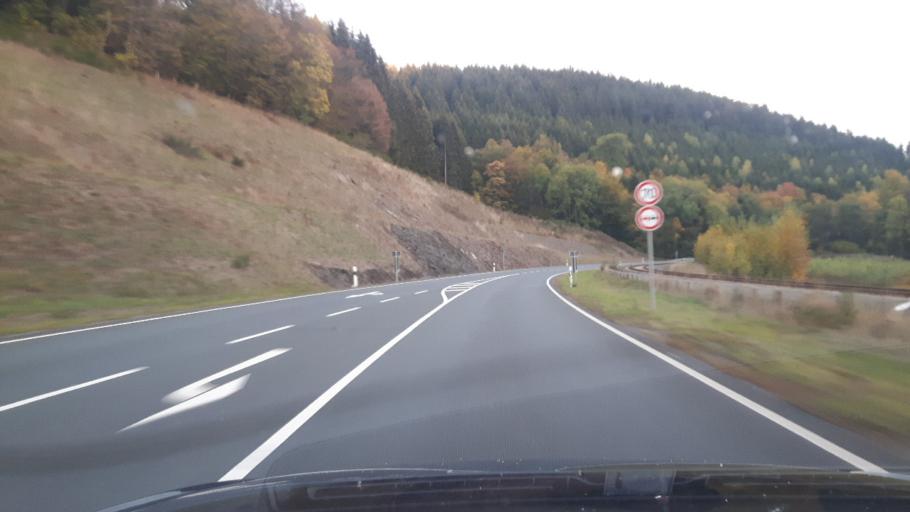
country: DE
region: North Rhine-Westphalia
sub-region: Regierungsbezirk Arnsberg
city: Bad Laasphe
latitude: 50.9489
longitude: 8.3731
